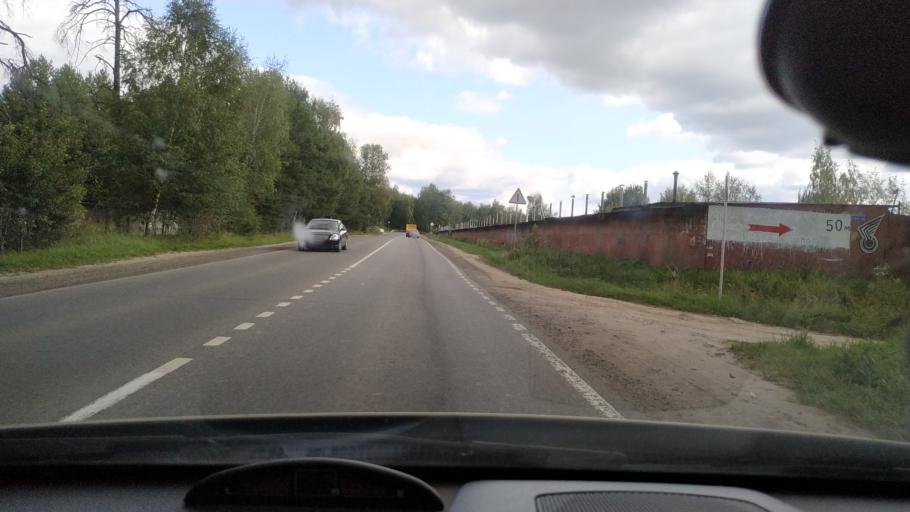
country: RU
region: Moskovskaya
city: Chornaya
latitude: 55.7657
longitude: 38.0670
